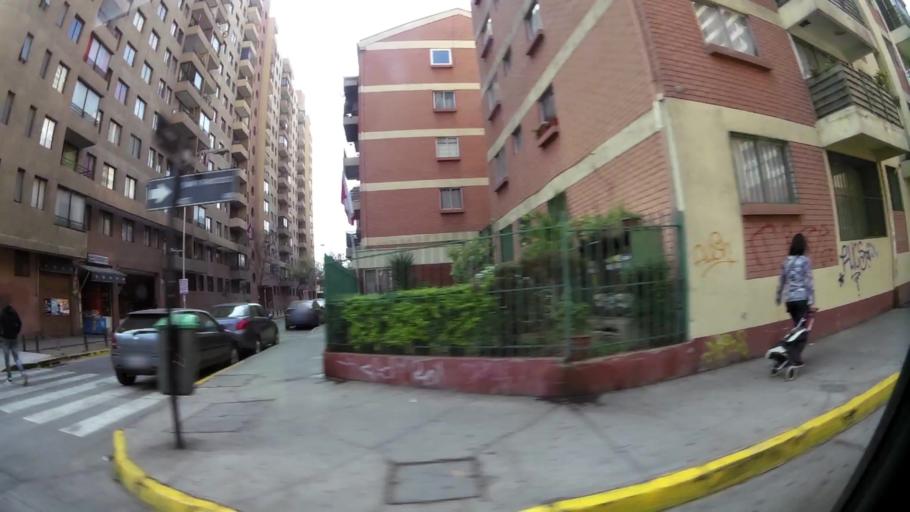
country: CL
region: Santiago Metropolitan
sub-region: Provincia de Santiago
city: Santiago
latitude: -33.4500
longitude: -70.6470
